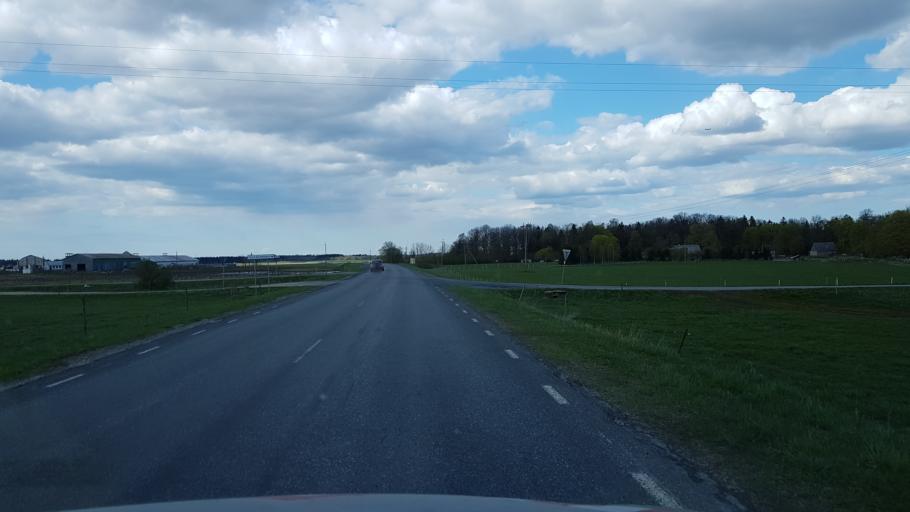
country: EE
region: Harju
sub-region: Keila linn
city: Keila
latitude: 59.2740
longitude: 24.4526
